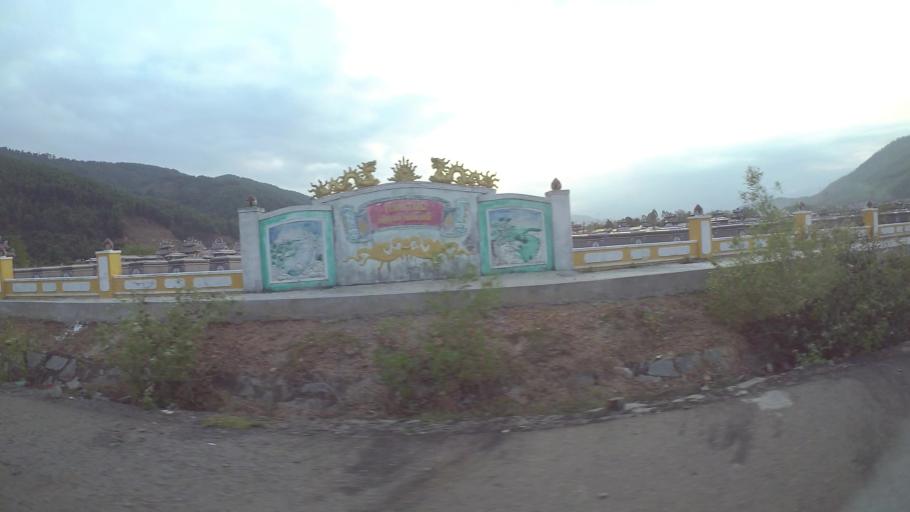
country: VN
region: Da Nang
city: Lien Chieu
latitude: 16.0578
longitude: 108.1268
